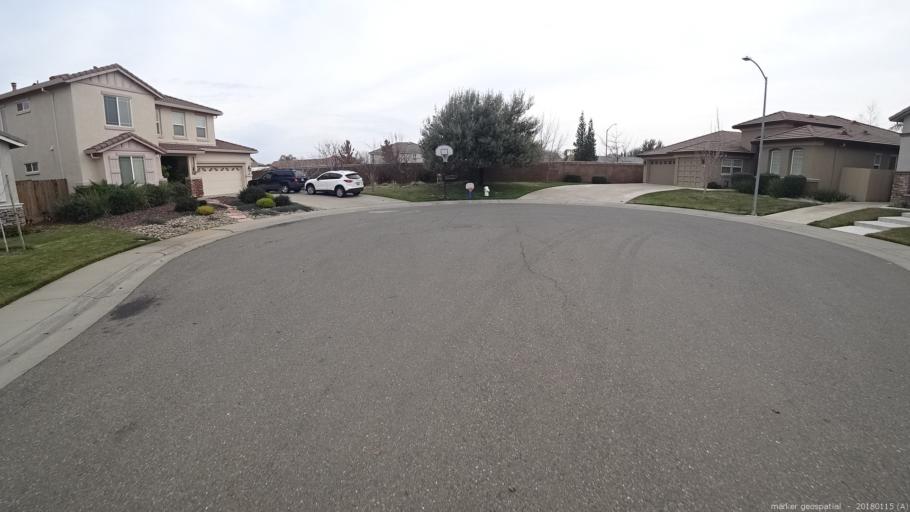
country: US
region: California
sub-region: Sacramento County
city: Rancho Cordova
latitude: 38.5802
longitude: -121.2760
